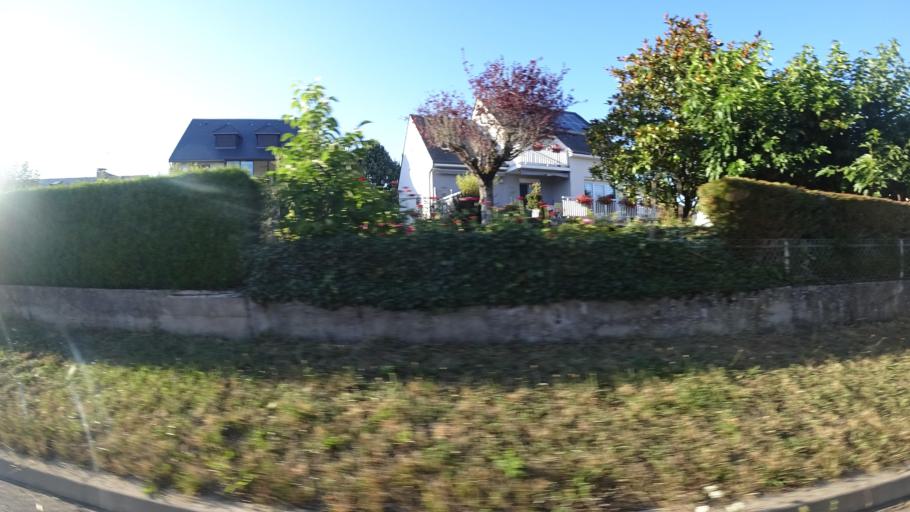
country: FR
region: Midi-Pyrenees
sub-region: Departement de l'Aveyron
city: Luc-la-Primaube
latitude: 44.3151
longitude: 2.5267
